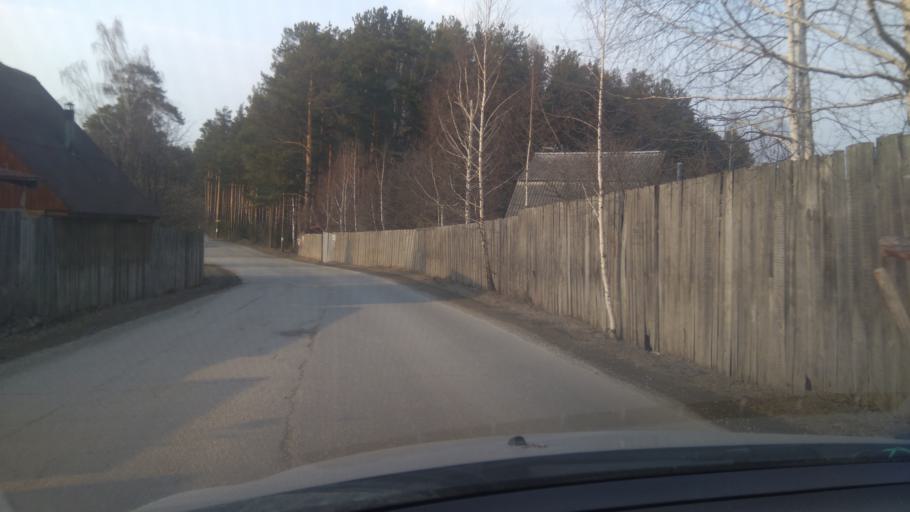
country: RU
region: Sverdlovsk
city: Severka
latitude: 56.8533
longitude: 60.3869
